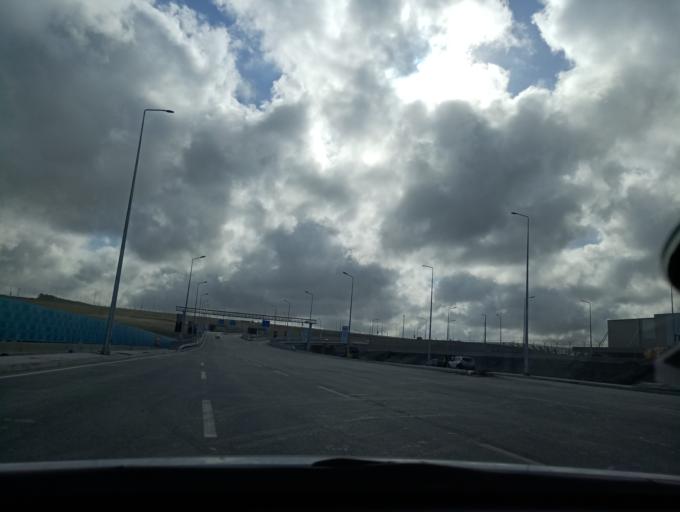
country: TR
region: Istanbul
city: Durusu
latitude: 41.2502
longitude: 28.7390
